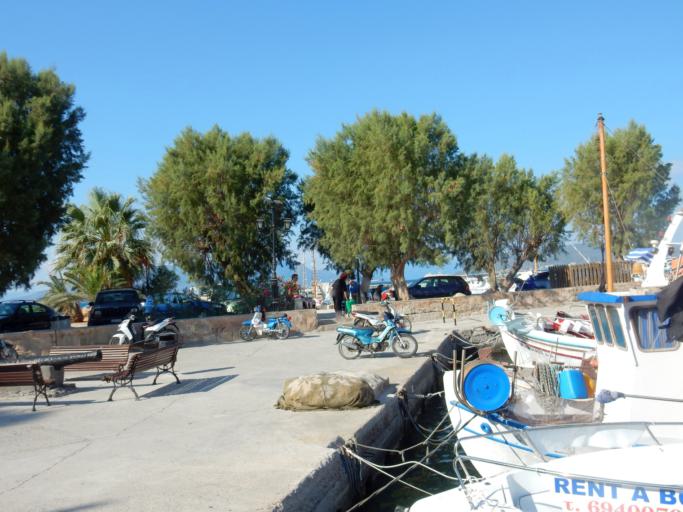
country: GR
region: Attica
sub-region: Nomos Piraios
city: Aegina
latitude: 37.7439
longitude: 23.4295
